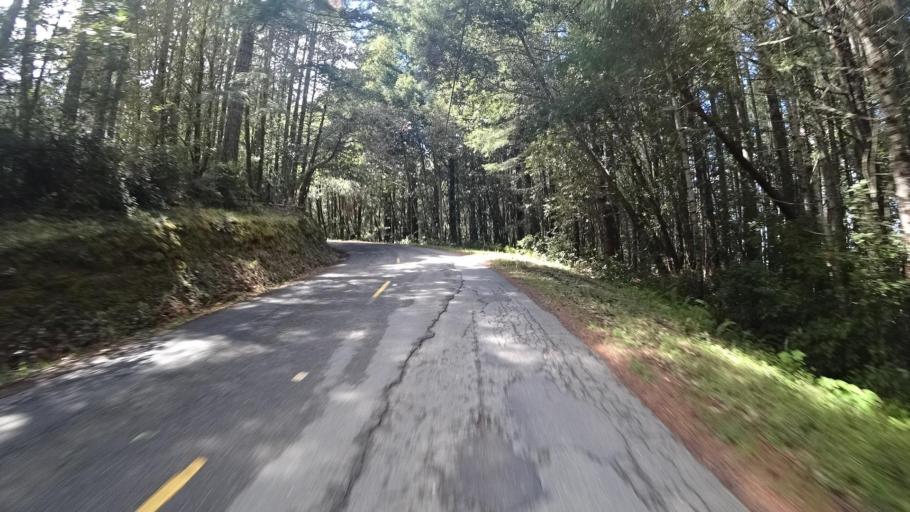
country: US
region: California
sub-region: Humboldt County
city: Blue Lake
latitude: 40.7613
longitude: -123.9619
